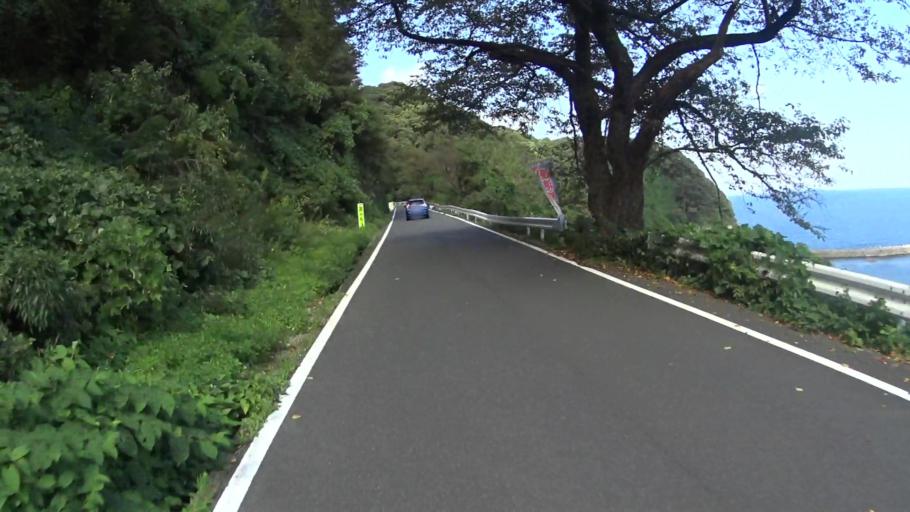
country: JP
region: Kyoto
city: Miyazu
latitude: 35.7539
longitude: 135.2499
